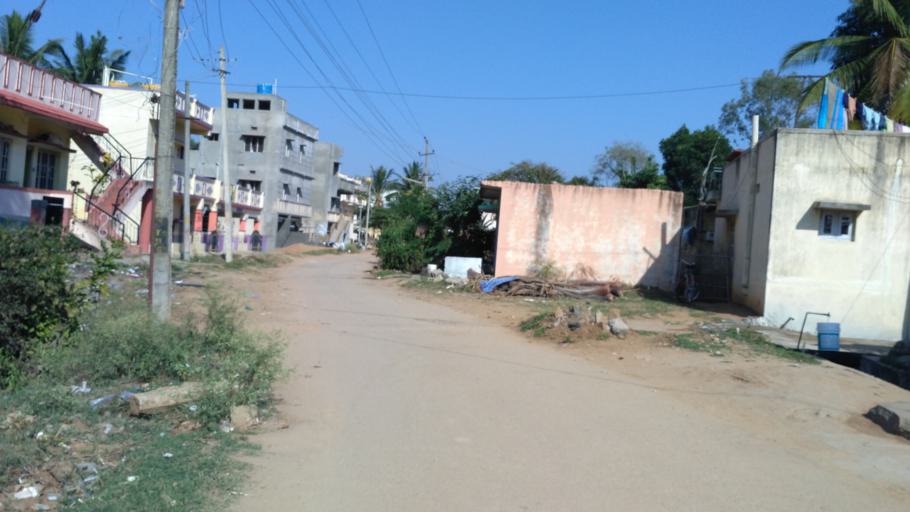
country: IN
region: Karnataka
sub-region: Hassan
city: Hassan
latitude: 13.0002
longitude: 76.1183
